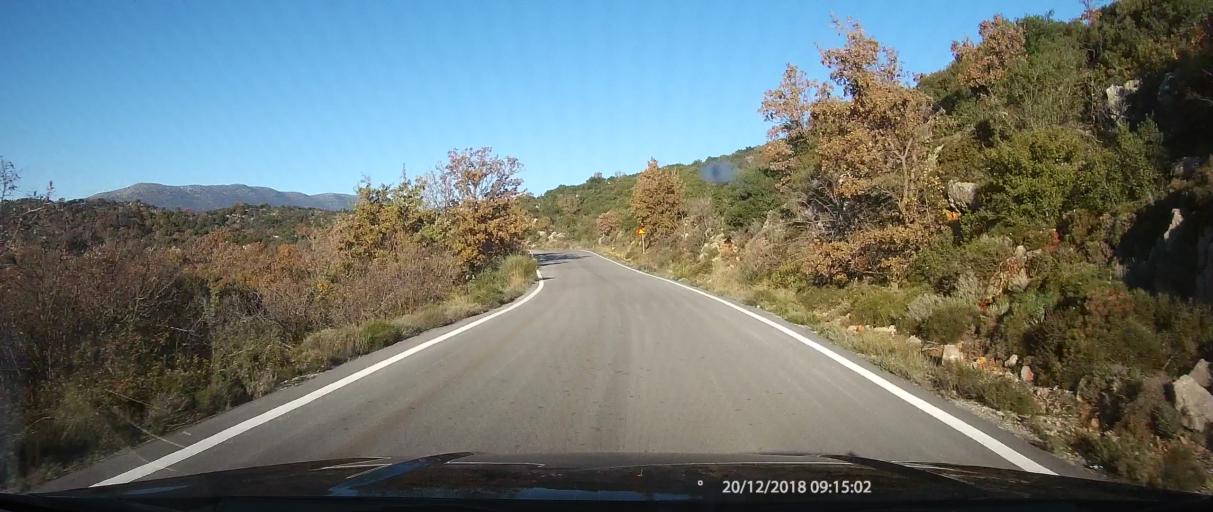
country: GR
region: Peloponnese
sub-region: Nomos Lakonias
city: Sykea
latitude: 36.9028
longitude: 22.9815
